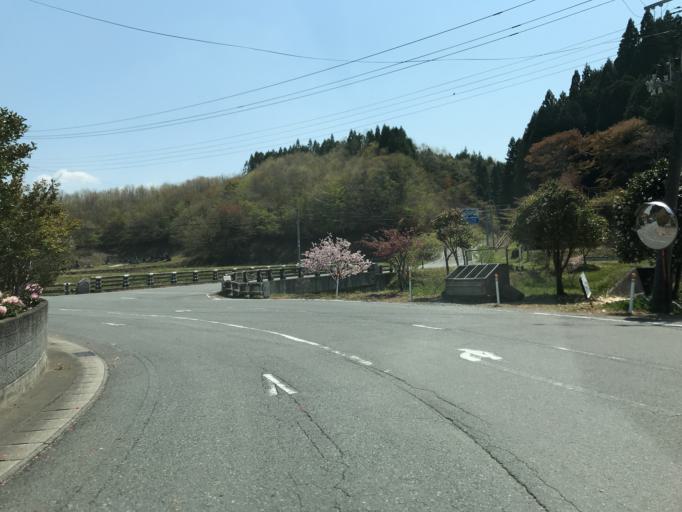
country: JP
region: Ibaraki
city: Kitaibaraki
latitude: 36.9579
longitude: 140.6679
